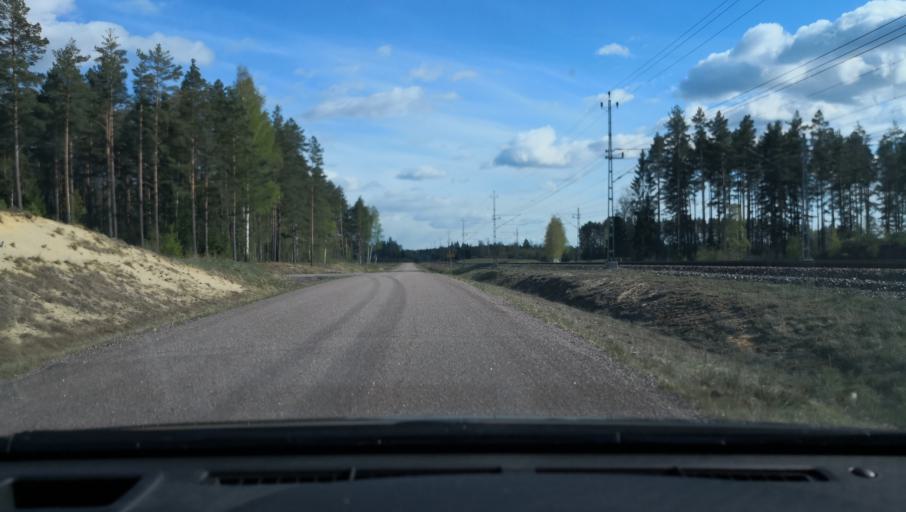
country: SE
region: OErebro
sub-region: Askersunds Kommun
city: Asbro
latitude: 58.9368
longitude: 15.0425
